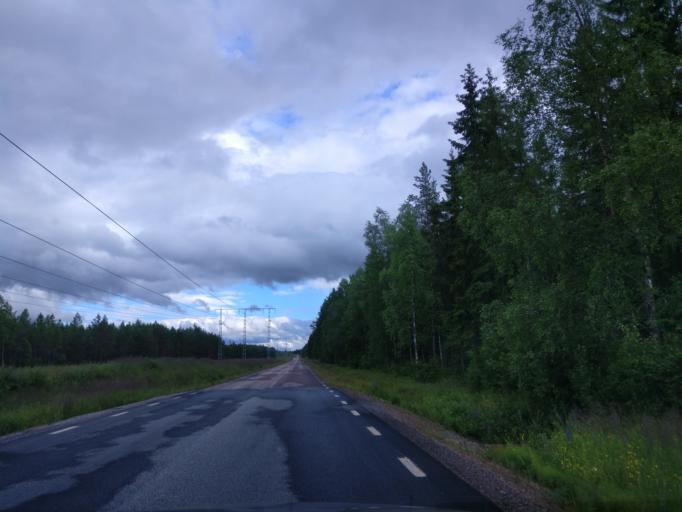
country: SE
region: Vaermland
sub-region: Hagfors Kommun
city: Hagfors
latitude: 60.0404
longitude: 13.5379
